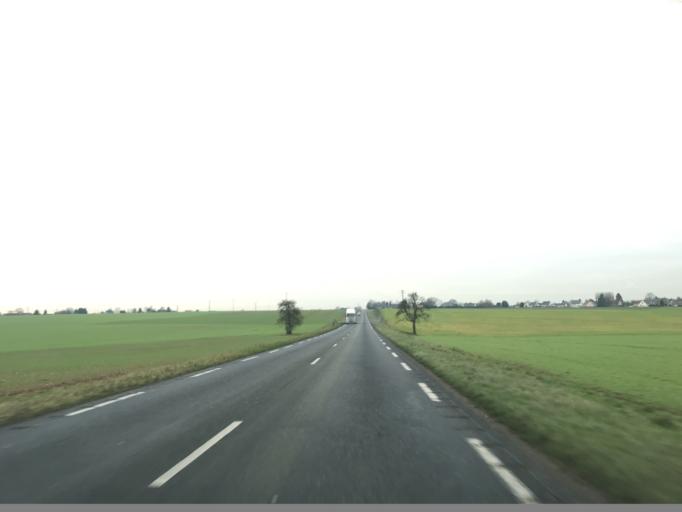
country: FR
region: Haute-Normandie
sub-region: Departement de la Seine-Maritime
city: Montmain
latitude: 49.3863
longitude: 1.2372
